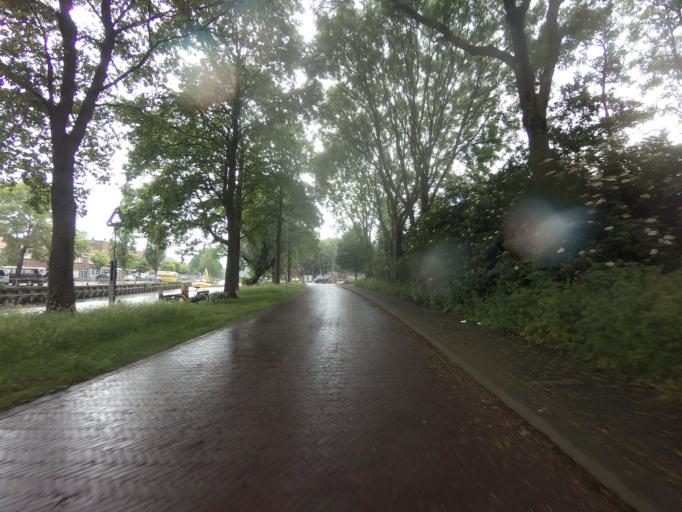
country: NL
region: Utrecht
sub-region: Gemeente Utrecht
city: Utrecht
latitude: 52.1080
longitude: 5.1065
